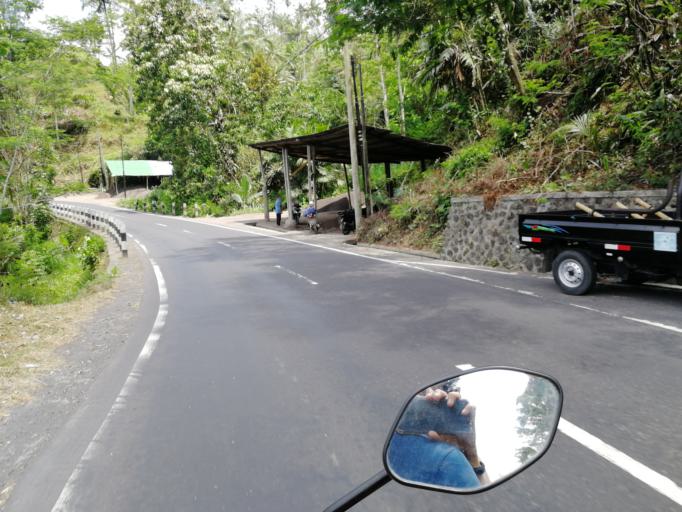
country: ID
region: Bali
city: Banjar Geriana Kangin
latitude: -8.4233
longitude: 115.4362
